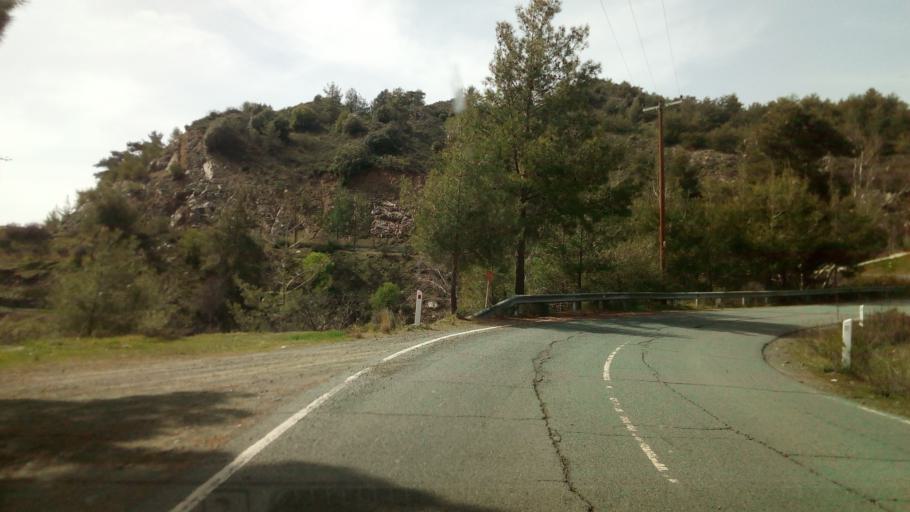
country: CY
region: Limassol
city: Pelendri
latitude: 34.8944
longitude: 32.9807
